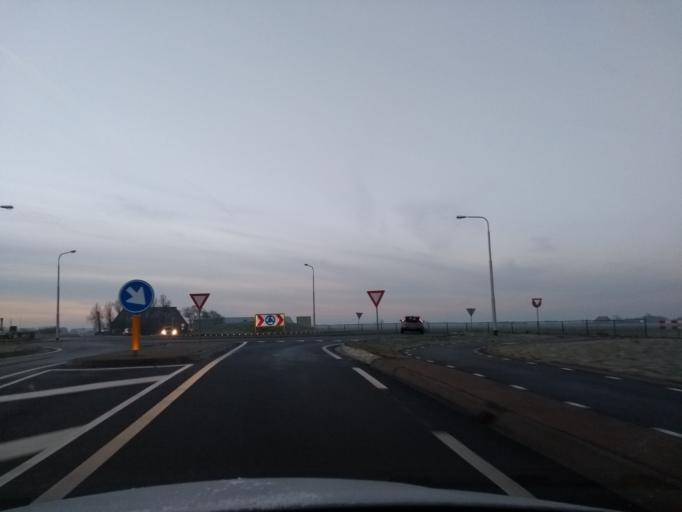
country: NL
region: Friesland
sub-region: Sudwest Fryslan
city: Woudsend
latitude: 52.9642
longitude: 5.6516
